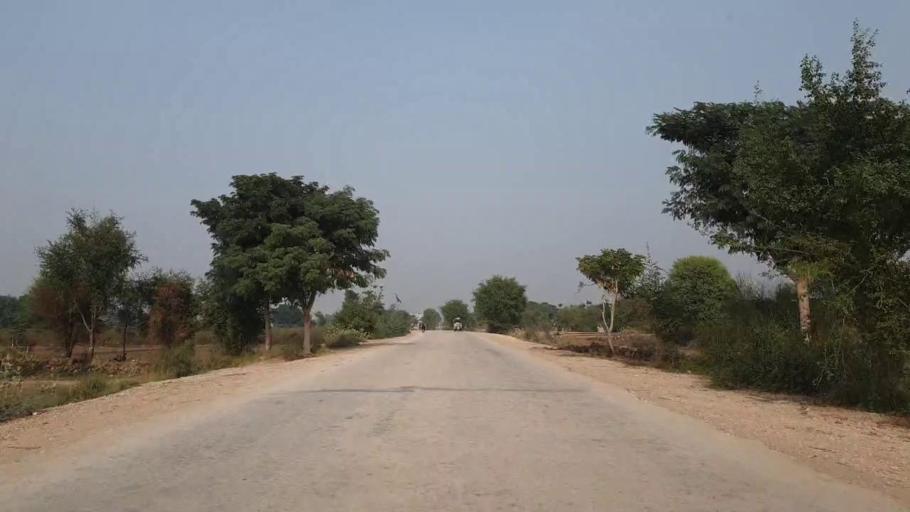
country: PK
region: Sindh
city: Bhan
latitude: 26.5720
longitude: 67.7269
